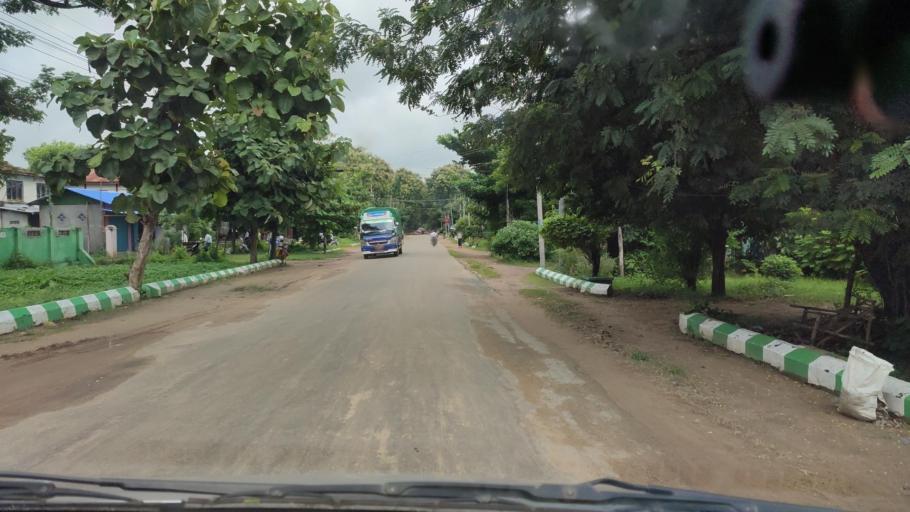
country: MM
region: Bago
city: Pyay
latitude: 18.9087
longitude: 95.5419
